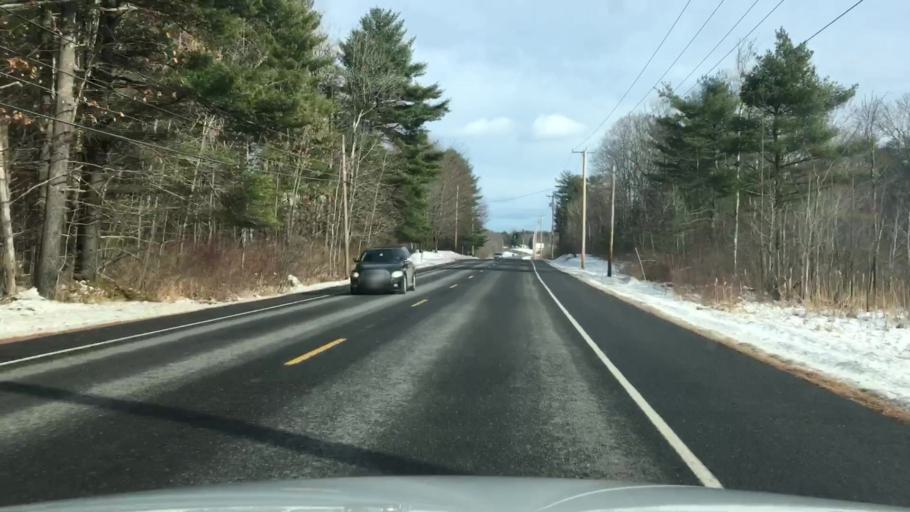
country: US
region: Maine
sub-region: Androscoggin County
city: Greene
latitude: 44.2008
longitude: -70.1146
